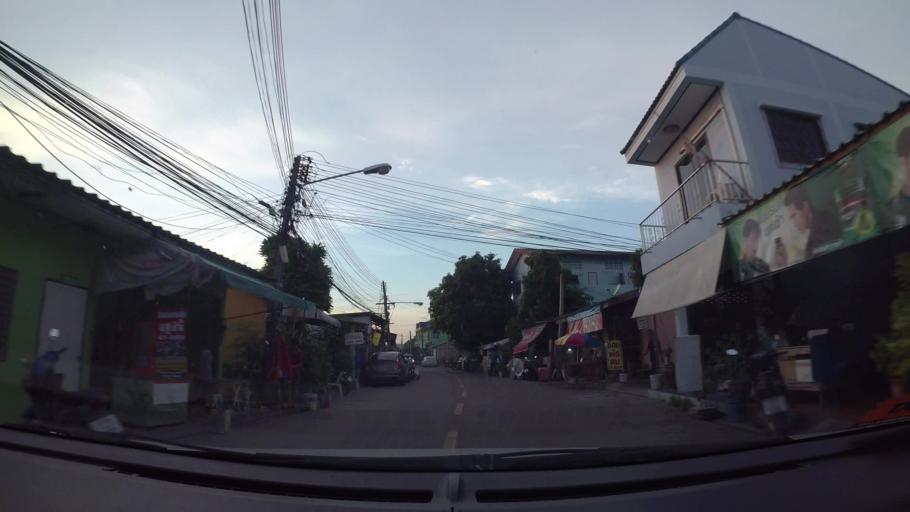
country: TH
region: Chon Buri
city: Chon Buri
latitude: 13.3967
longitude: 100.9860
